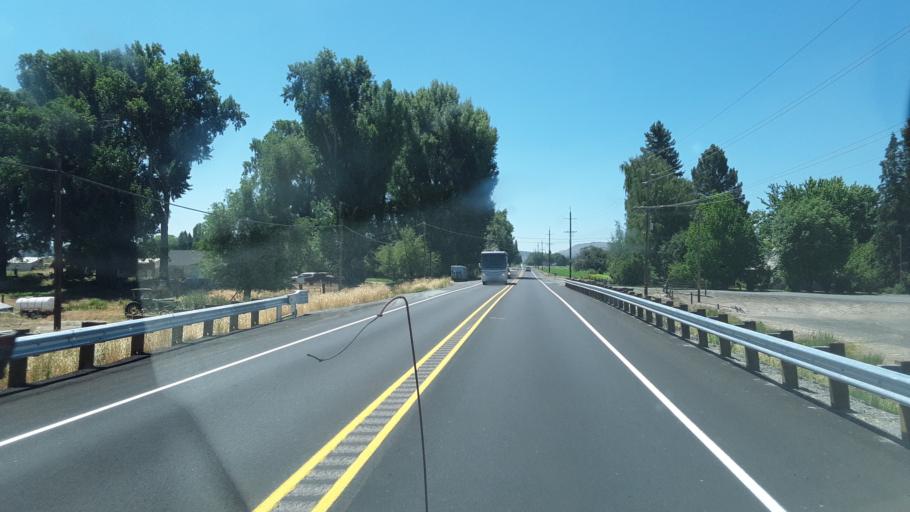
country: US
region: Oregon
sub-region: Klamath County
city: Altamont
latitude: 42.1402
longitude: -121.6984
